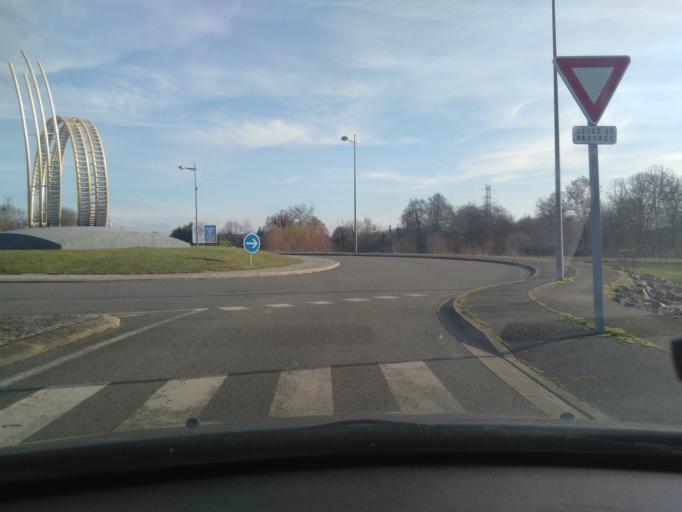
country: FR
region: Centre
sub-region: Departement du Cher
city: Saint-Amand-Montrond
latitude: 46.7216
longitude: 2.5297
